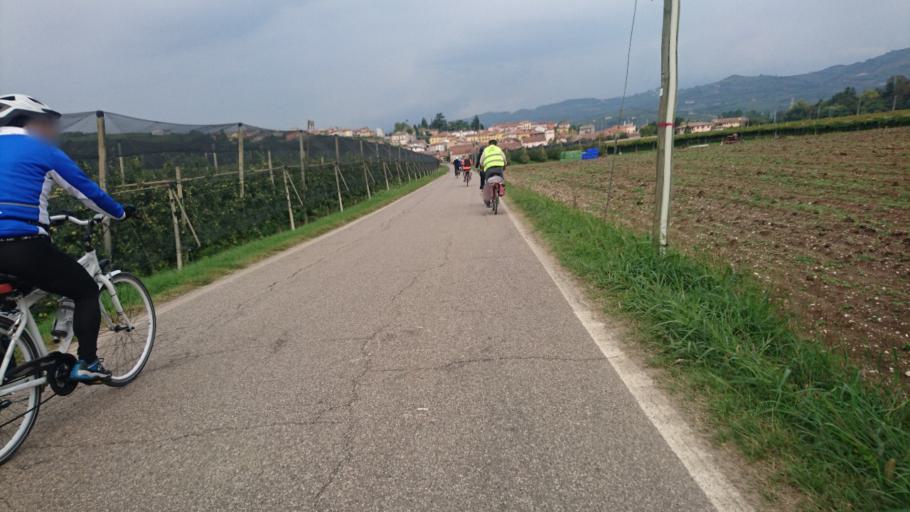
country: IT
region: Veneto
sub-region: Provincia di Verona
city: Soave
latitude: 45.4240
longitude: 11.2214
